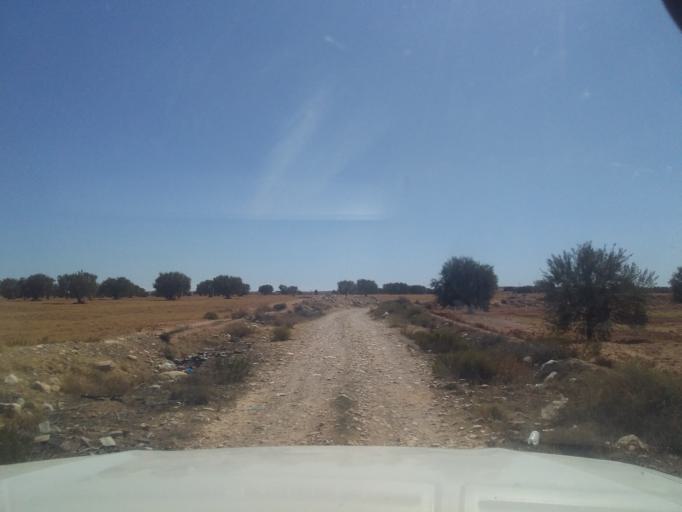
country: TN
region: Qabis
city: Matmata
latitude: 33.5836
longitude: 10.2830
